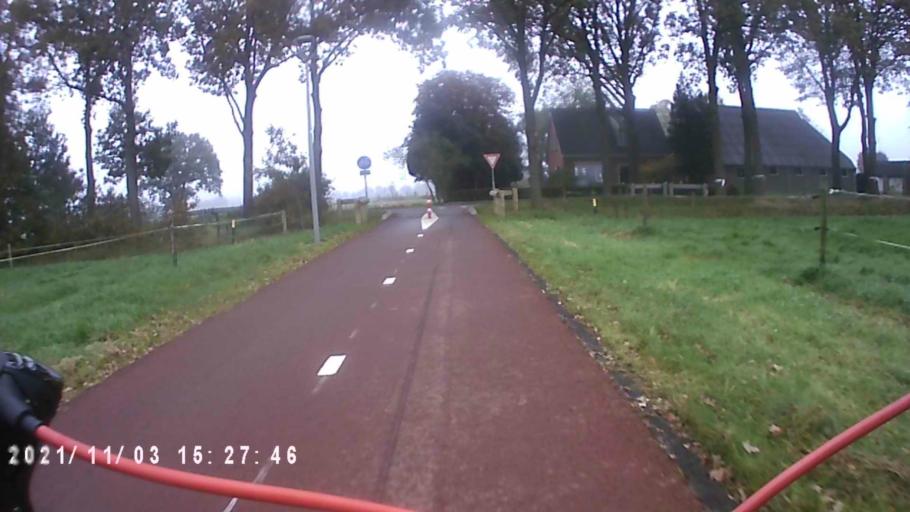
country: NL
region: Groningen
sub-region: Gemeente Leek
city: Leek
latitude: 53.1406
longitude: 6.3760
